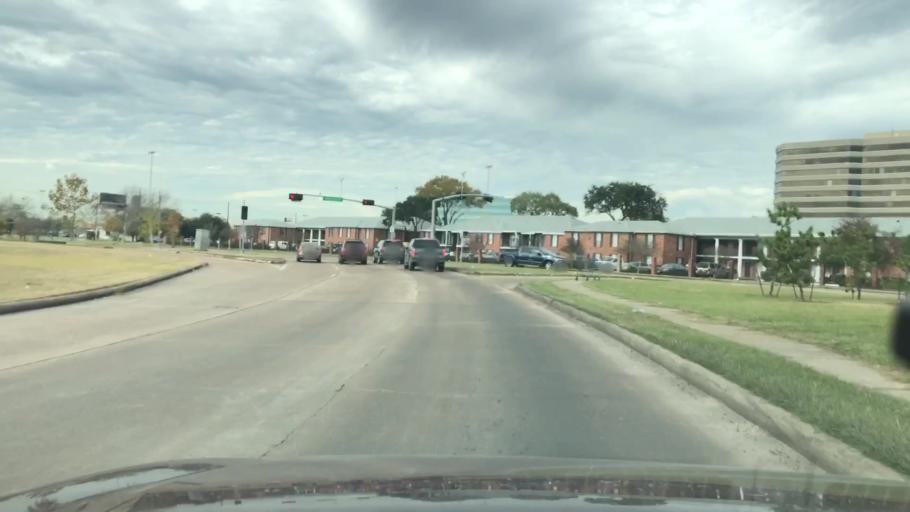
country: US
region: Texas
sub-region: Fort Bend County
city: Meadows Place
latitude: 29.6756
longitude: -95.5365
